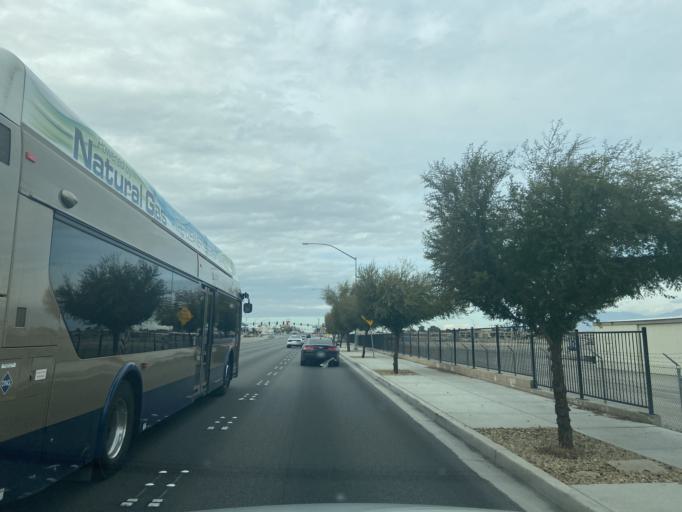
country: US
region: Nevada
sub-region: Clark County
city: Las Vegas
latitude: 36.2115
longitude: -115.2068
